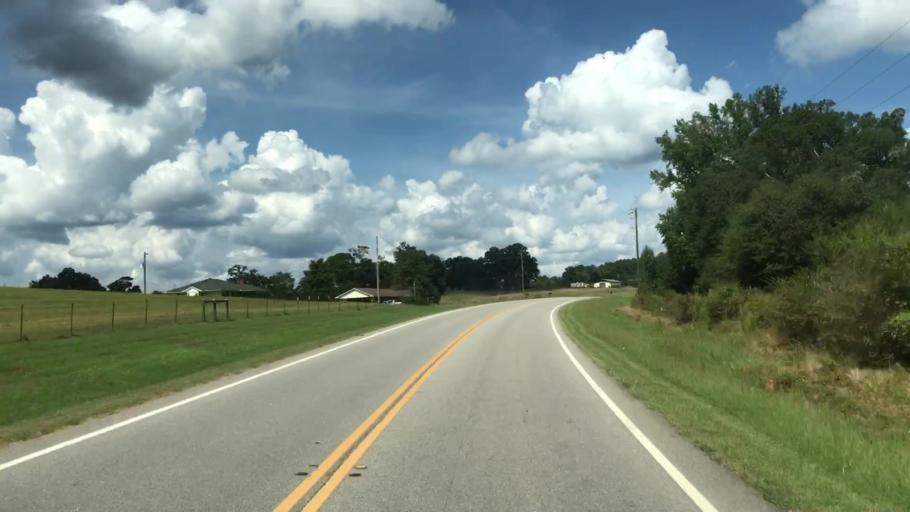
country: US
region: Georgia
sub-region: Greene County
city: Greensboro
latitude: 33.6447
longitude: -83.2316
